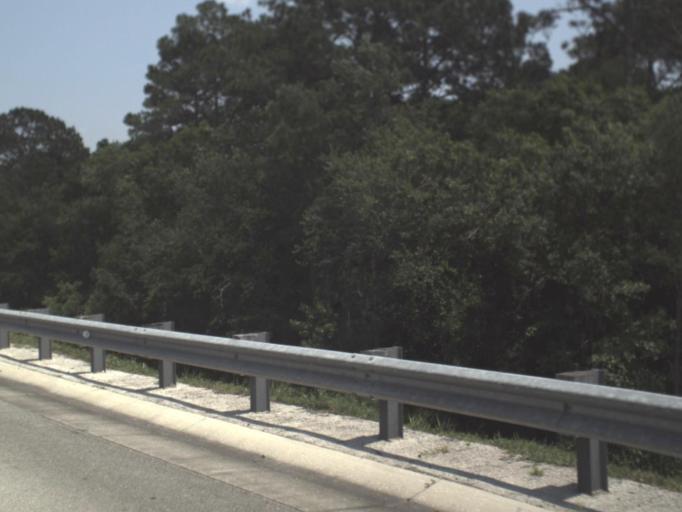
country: US
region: Florida
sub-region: Duval County
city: Baldwin
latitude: 30.2016
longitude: -82.0126
